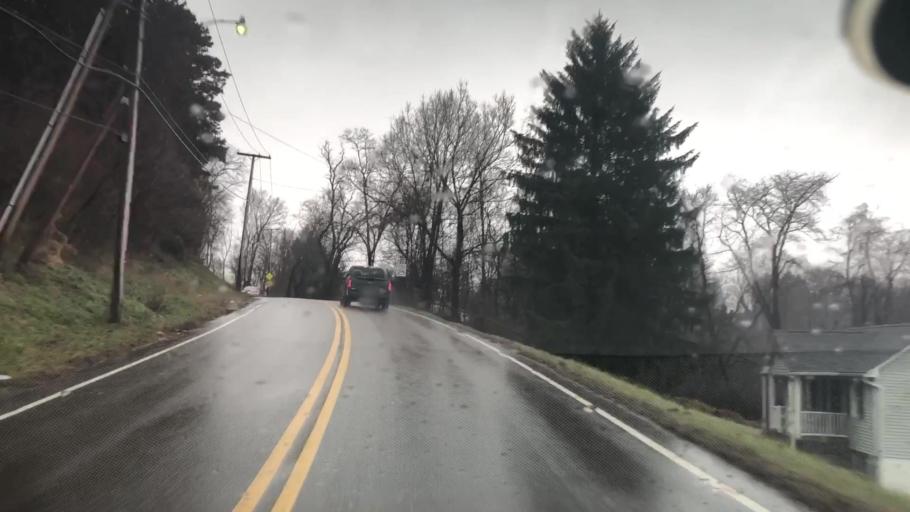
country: US
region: Ohio
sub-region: Belmont County
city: Saint Clairsville
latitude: 40.0819
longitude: -80.9073
